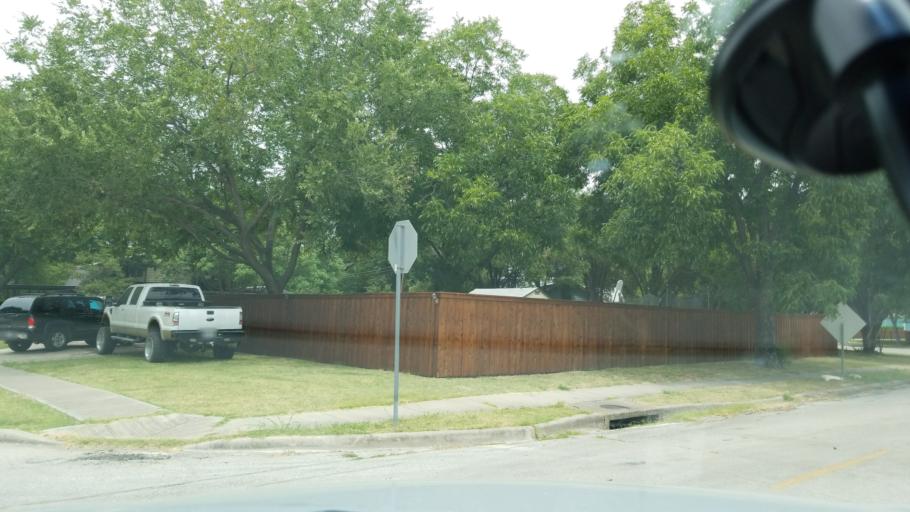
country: US
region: Texas
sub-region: Dallas County
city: Grand Prairie
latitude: 32.7408
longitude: -96.9893
